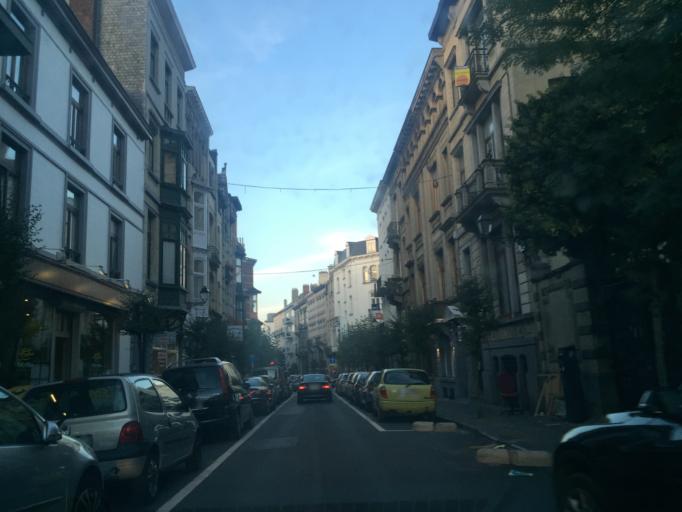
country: BE
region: Brussels Capital
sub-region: Bruxelles-Capitale
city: Brussels
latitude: 50.8356
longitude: 4.3638
